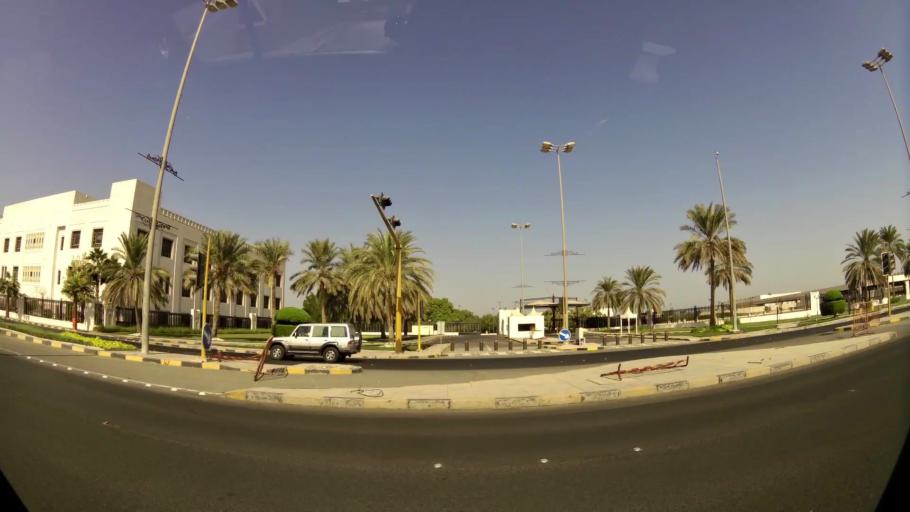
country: KW
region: Al Asimah
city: Kuwait City
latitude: 29.3751
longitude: 47.9673
